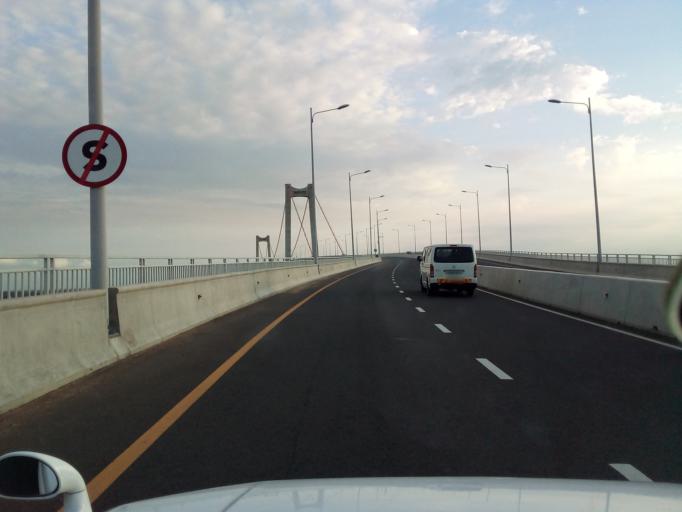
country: MZ
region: Maputo City
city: Maputo
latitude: -25.9647
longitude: 32.5609
